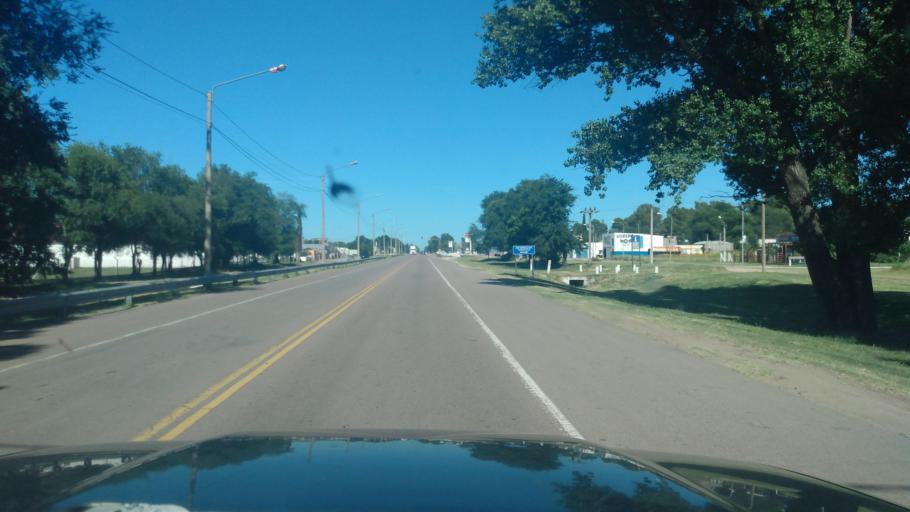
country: AR
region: La Pampa
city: General Acha
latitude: -37.3662
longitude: -64.5954
